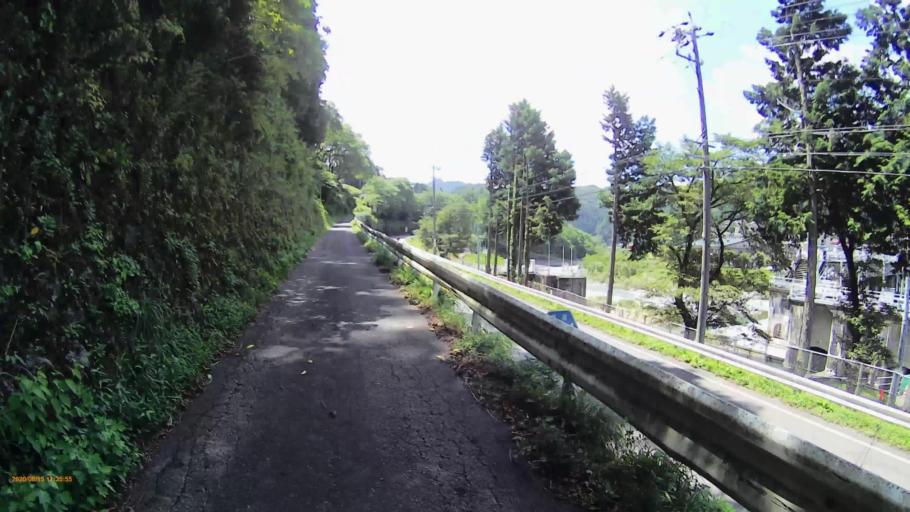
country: JP
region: Nagano
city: Ina
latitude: 35.8362
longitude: 137.6871
